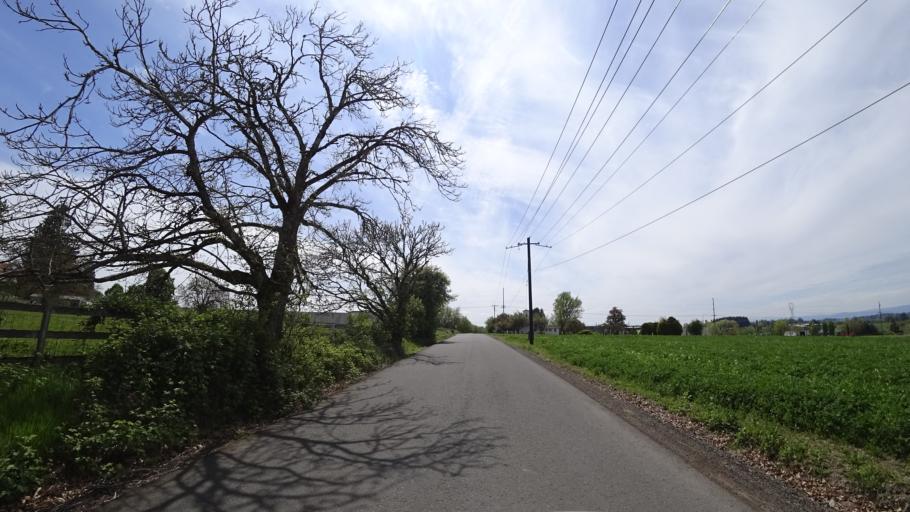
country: US
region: Oregon
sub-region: Washington County
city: Rockcreek
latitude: 45.5750
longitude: -122.9059
